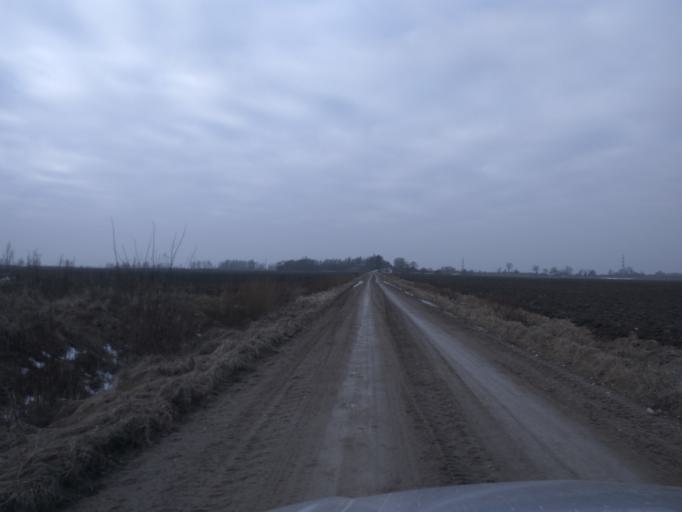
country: LV
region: Durbe
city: Liegi
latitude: 56.6697
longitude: 21.3725
